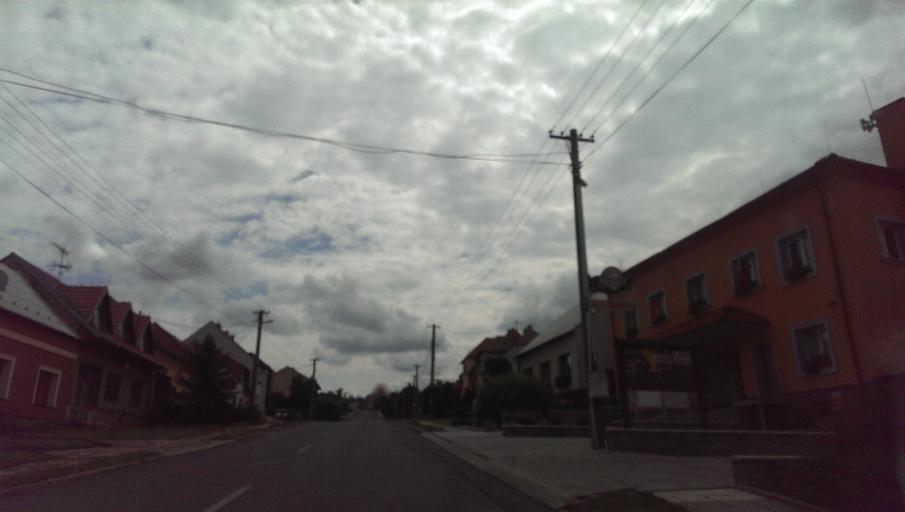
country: CZ
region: South Moravian
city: Velka nad Velickou
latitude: 48.9067
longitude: 17.5634
